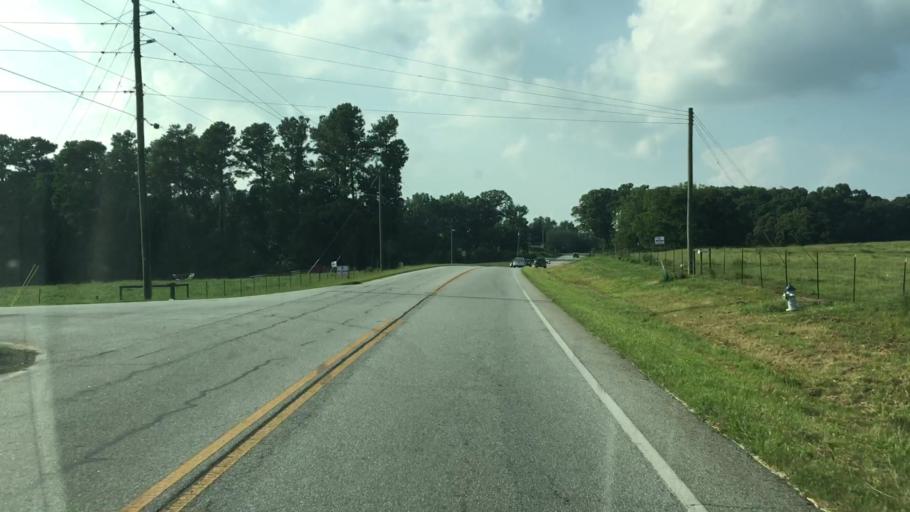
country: US
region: Georgia
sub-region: Jackson County
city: Braselton
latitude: 34.1418
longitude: -83.7953
